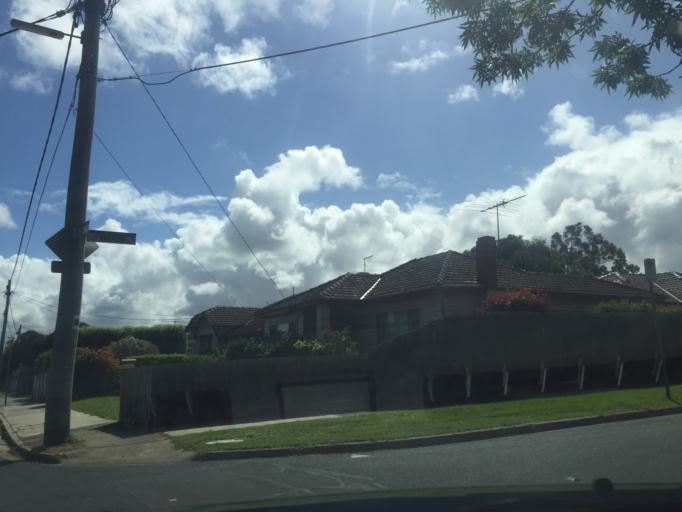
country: AU
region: Victoria
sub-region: Banyule
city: Bellfield
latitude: -37.7632
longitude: 145.0313
